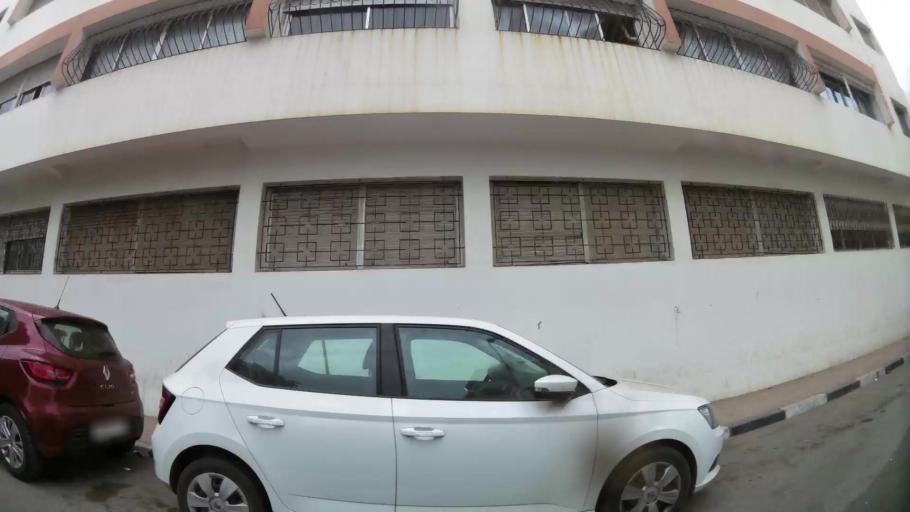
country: MA
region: Rabat-Sale-Zemmour-Zaer
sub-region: Rabat
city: Rabat
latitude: 33.9921
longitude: -6.8822
